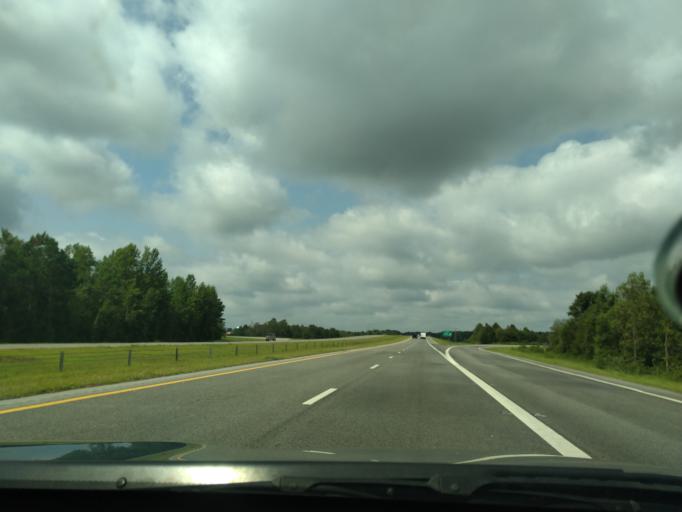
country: US
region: North Carolina
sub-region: Martin County
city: Robersonville
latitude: 35.8386
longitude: -77.2460
